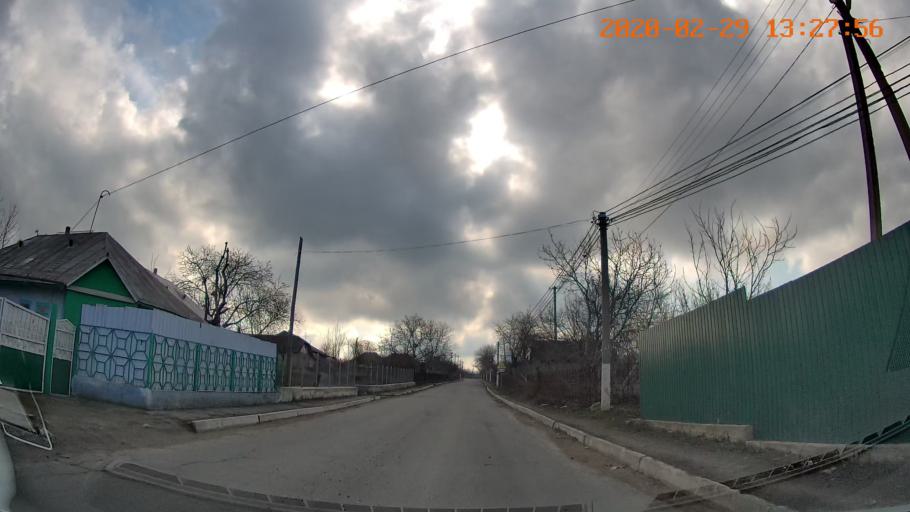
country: MD
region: Telenesti
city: Camenca
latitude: 47.9092
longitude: 28.6447
